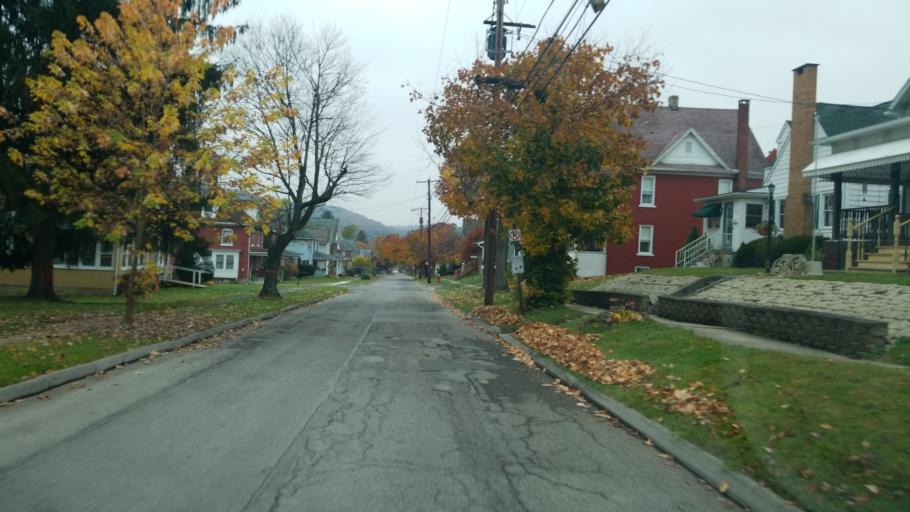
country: US
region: Pennsylvania
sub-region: Clearfield County
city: Clearfield
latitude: 41.0131
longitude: -78.4351
